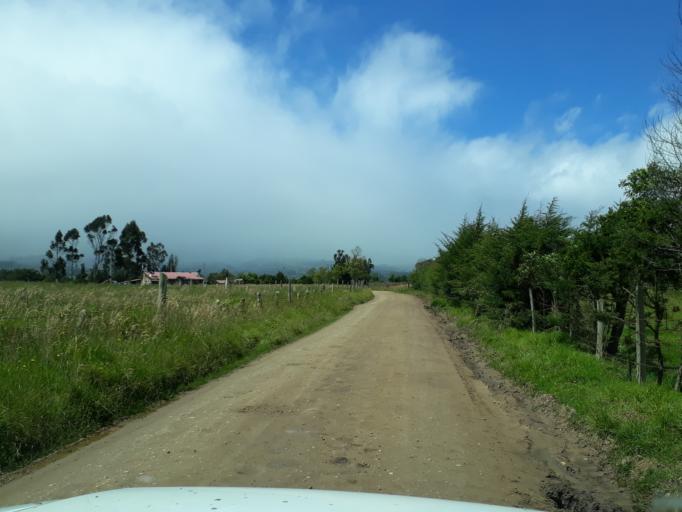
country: CO
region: Cundinamarca
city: Guasca
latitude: 4.8796
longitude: -73.8820
